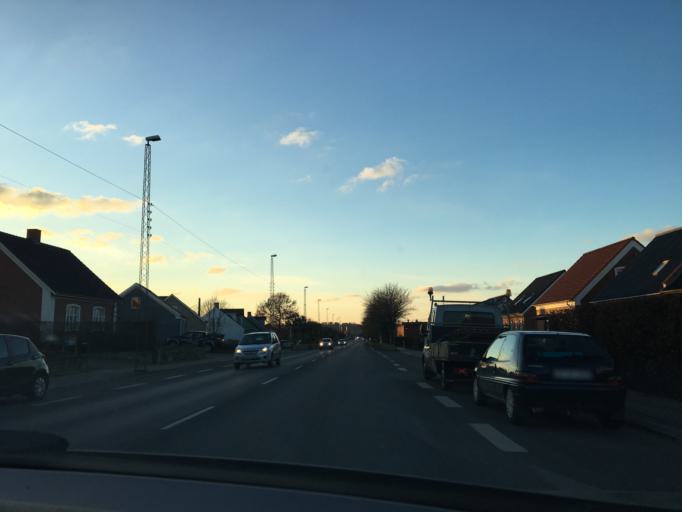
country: DK
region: South Denmark
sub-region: Middelfart Kommune
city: Middelfart
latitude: 55.4999
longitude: 9.7560
